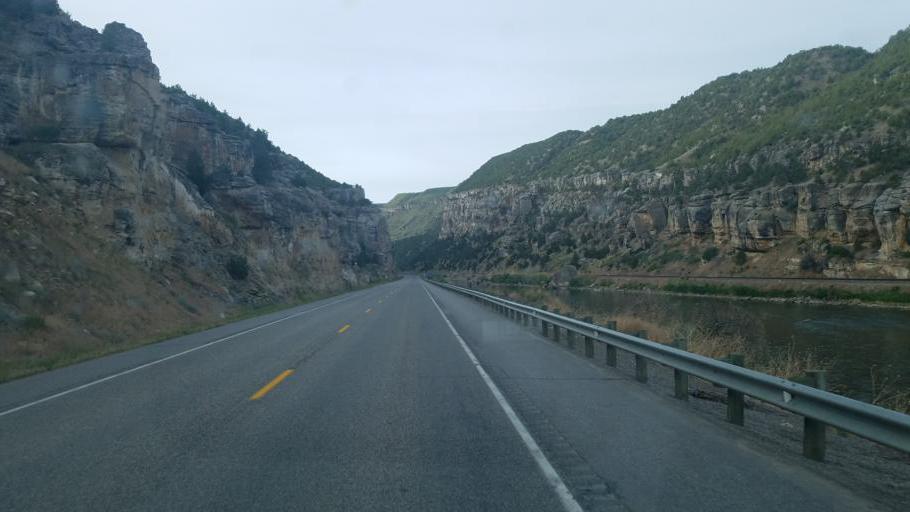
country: US
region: Wyoming
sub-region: Hot Springs County
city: Thermopolis
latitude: 43.5768
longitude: -108.2120
